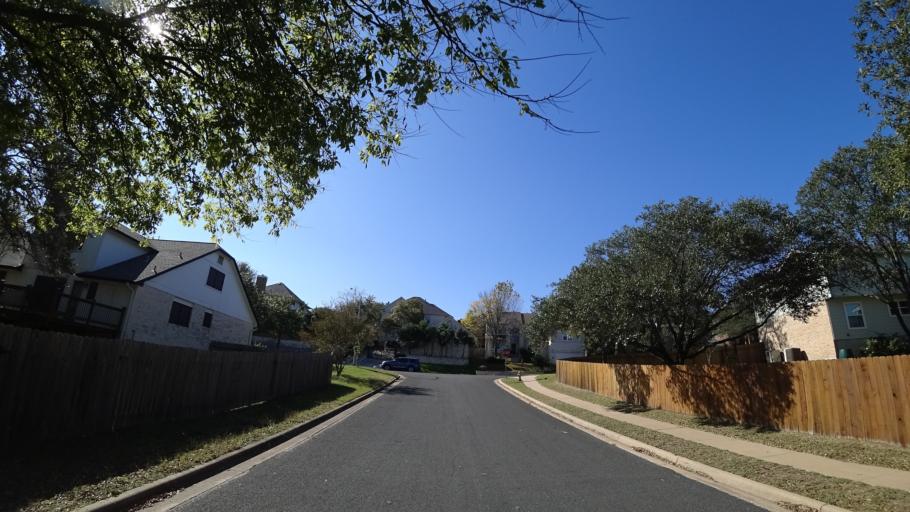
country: US
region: Texas
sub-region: Williamson County
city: Jollyville
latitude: 30.4174
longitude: -97.7610
